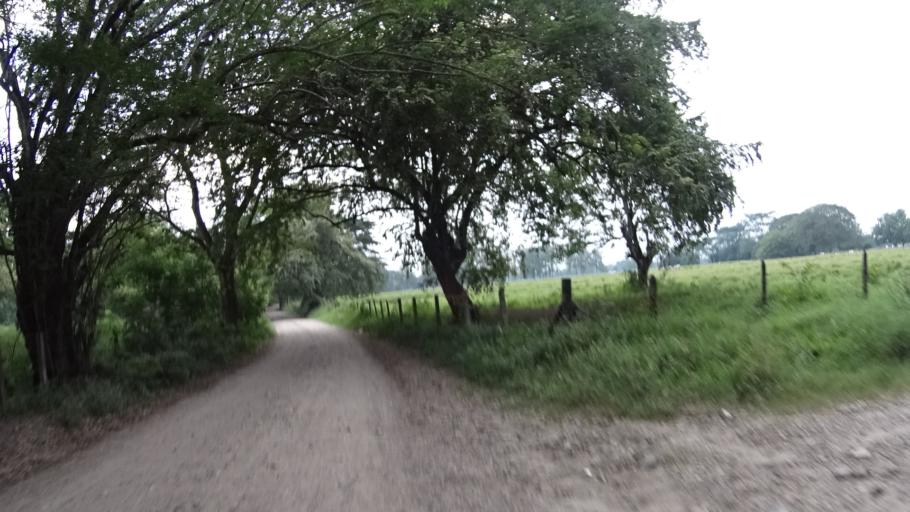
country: CO
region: Cundinamarca
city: Puerto Salgar
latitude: 5.4813
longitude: -74.6823
